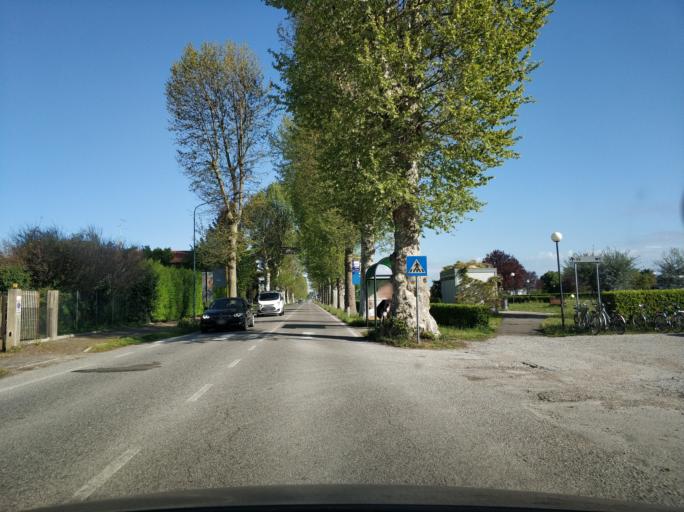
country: IT
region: Friuli Venezia Giulia
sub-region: Provincia di Udine
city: Aquileia
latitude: 45.7755
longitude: 13.3649
